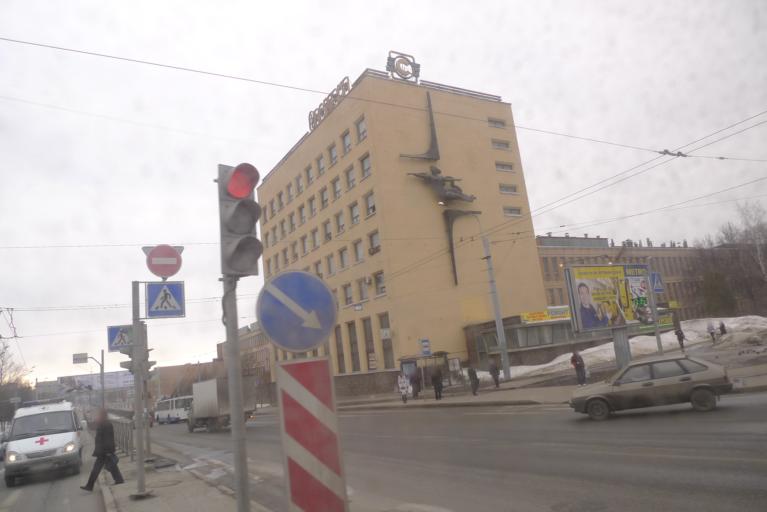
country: RU
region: St.-Petersburg
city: Sosnovka
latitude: 60.0106
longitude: 30.3468
